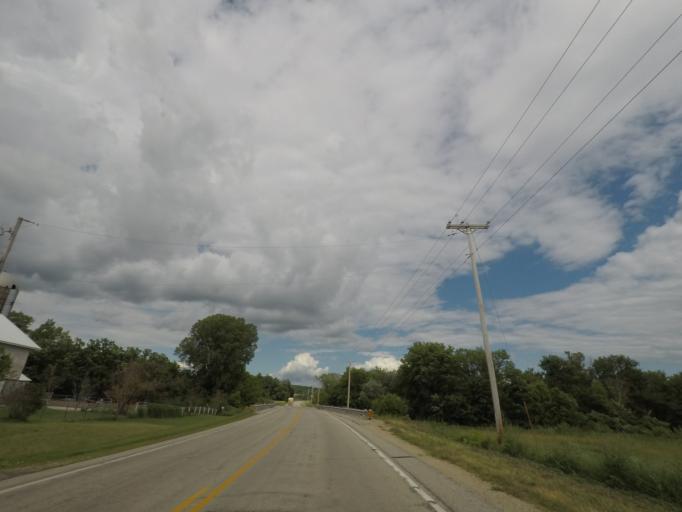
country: US
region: Wisconsin
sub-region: Dane County
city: Belleville
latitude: 42.8279
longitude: -89.4888
